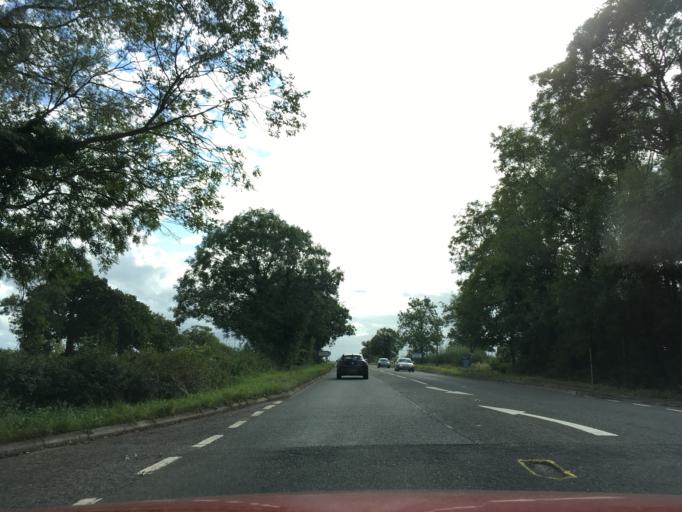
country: GB
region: England
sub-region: Gloucestershire
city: Berkeley
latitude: 51.6901
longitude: -2.4271
